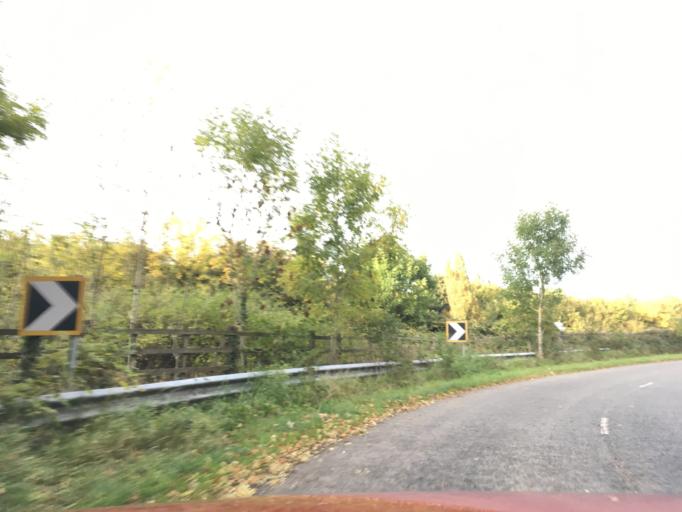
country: GB
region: England
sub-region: South Gloucestershire
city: Severn Beach
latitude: 51.5688
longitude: -2.6398
